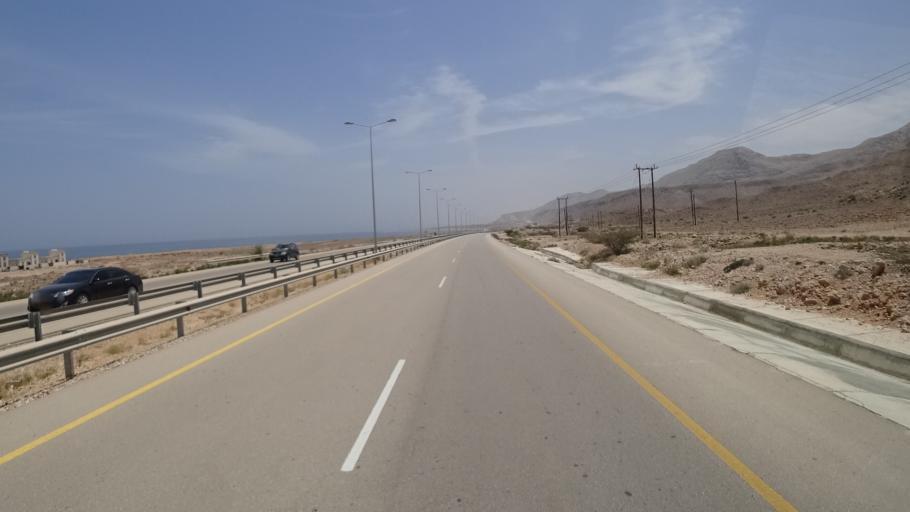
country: OM
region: Ash Sharqiyah
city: Sur
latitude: 22.7355
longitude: 59.3380
